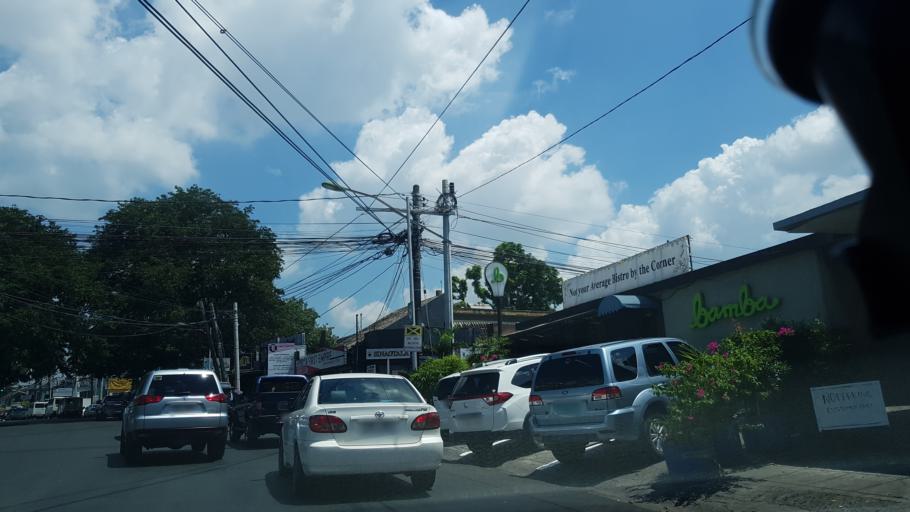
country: PH
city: Sambayanihan People's Village
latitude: 14.4450
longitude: 121.0238
